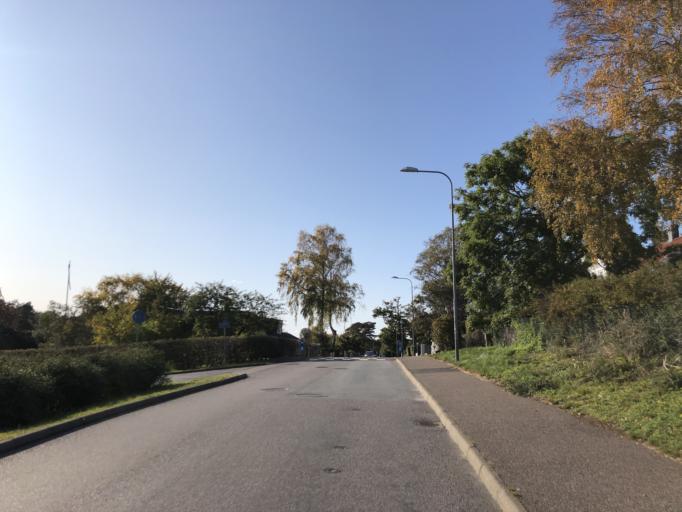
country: SE
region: Vaestra Goetaland
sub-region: Goteborg
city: Billdal
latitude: 57.6201
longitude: 11.8950
